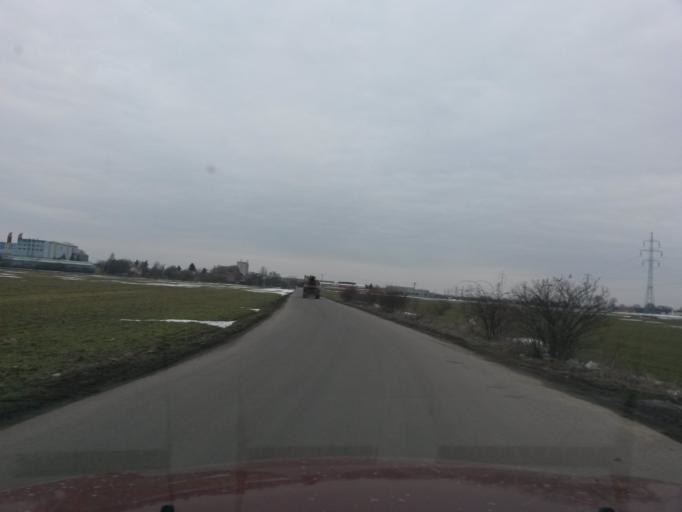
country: SK
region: Kosicky
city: Michalovce
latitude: 48.7430
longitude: 21.8872
